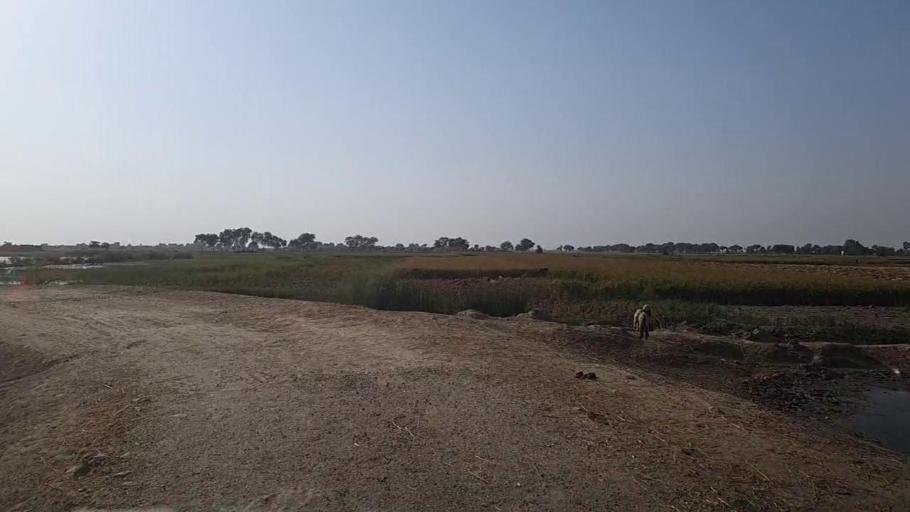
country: PK
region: Sindh
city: Kandhkot
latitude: 28.3672
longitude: 69.3301
